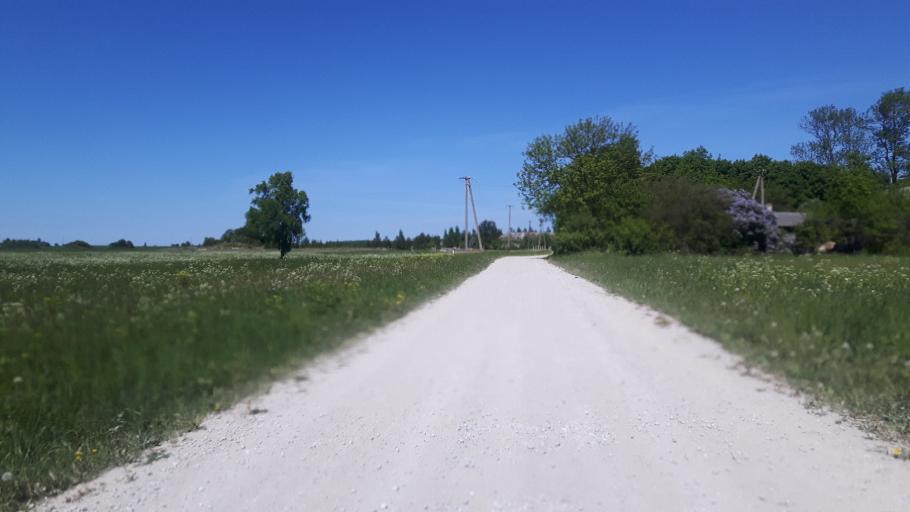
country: EE
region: Ida-Virumaa
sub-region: Toila vald
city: Voka
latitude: 59.3930
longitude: 27.6679
